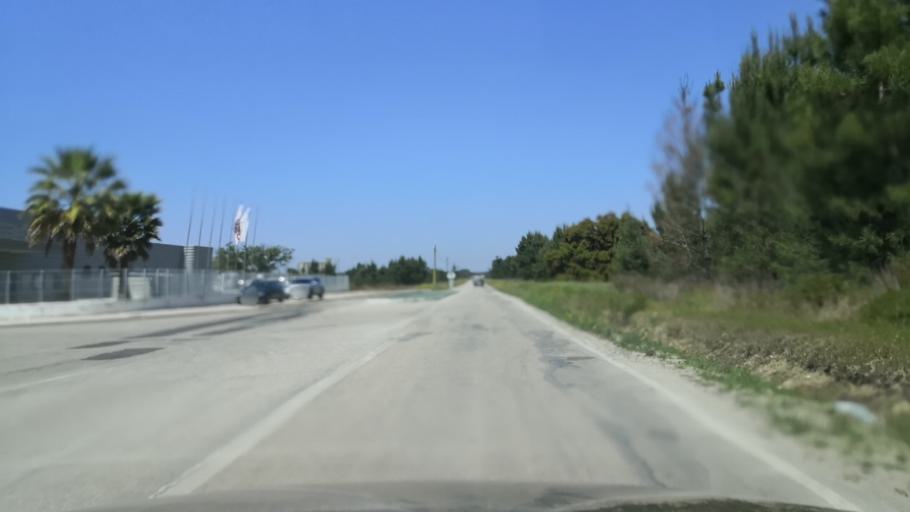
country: PT
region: Setubal
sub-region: Palmela
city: Palmela
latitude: 38.6231
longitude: -8.7465
